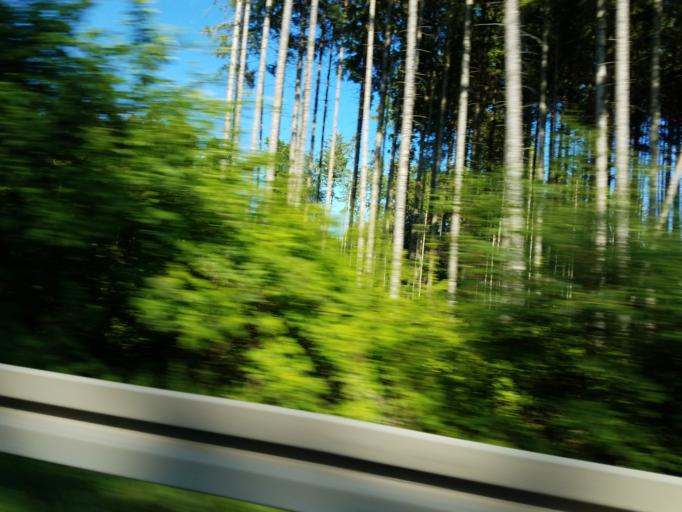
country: DE
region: Bavaria
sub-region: Upper Bavaria
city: Gilching
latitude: 48.0588
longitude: 11.3102
